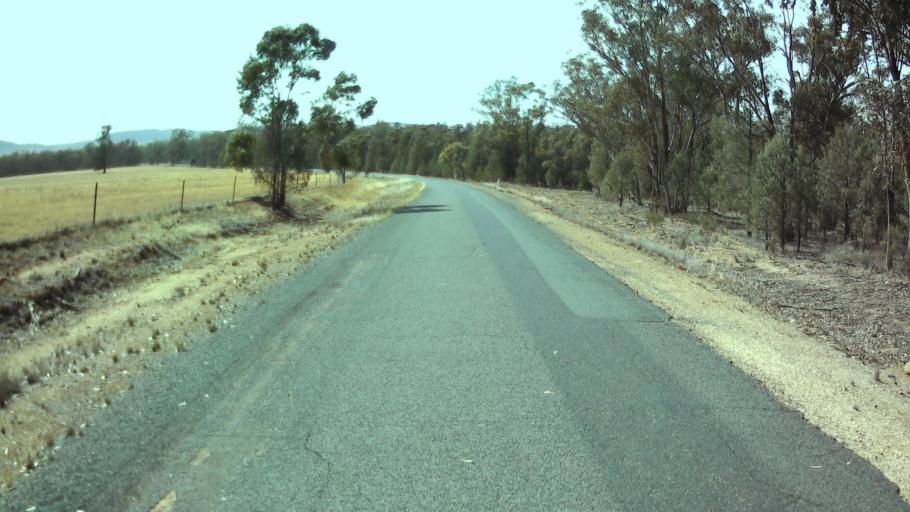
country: AU
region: New South Wales
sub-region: Weddin
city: Grenfell
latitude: -33.7553
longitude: 148.0739
